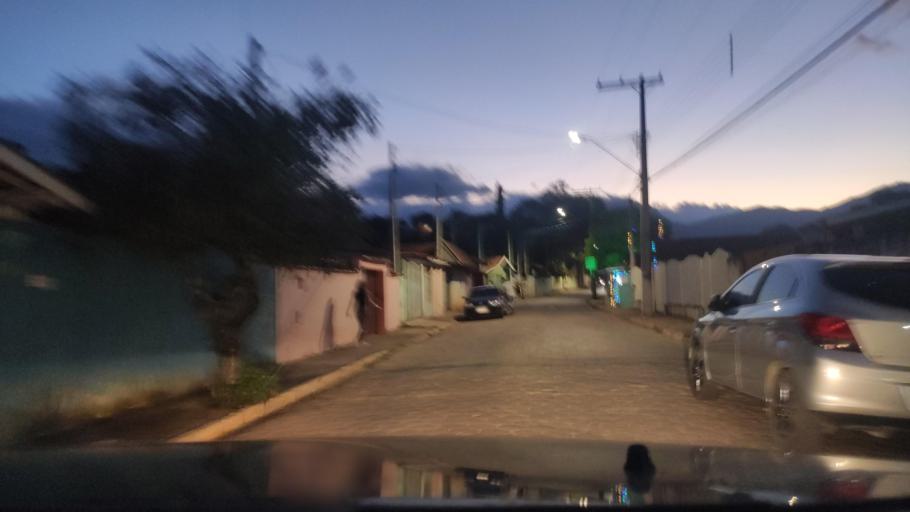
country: BR
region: Minas Gerais
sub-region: Paraisopolis
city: Paraisopolis
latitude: -22.6933
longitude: -45.7426
